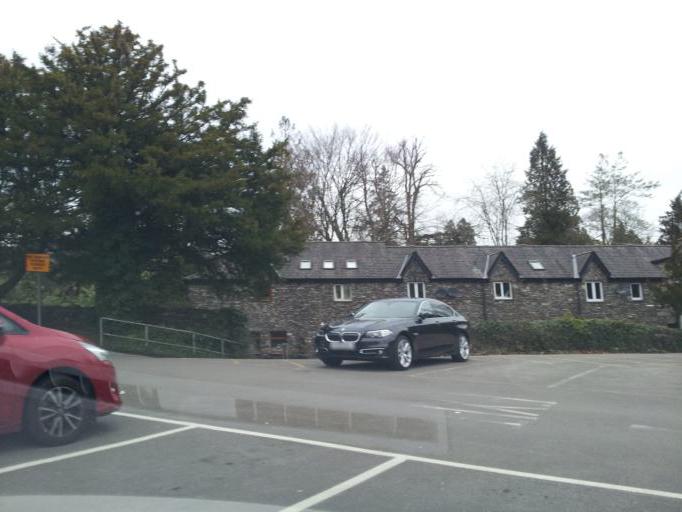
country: GB
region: England
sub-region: Cumbria
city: Windermere
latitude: 54.3653
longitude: -2.9206
